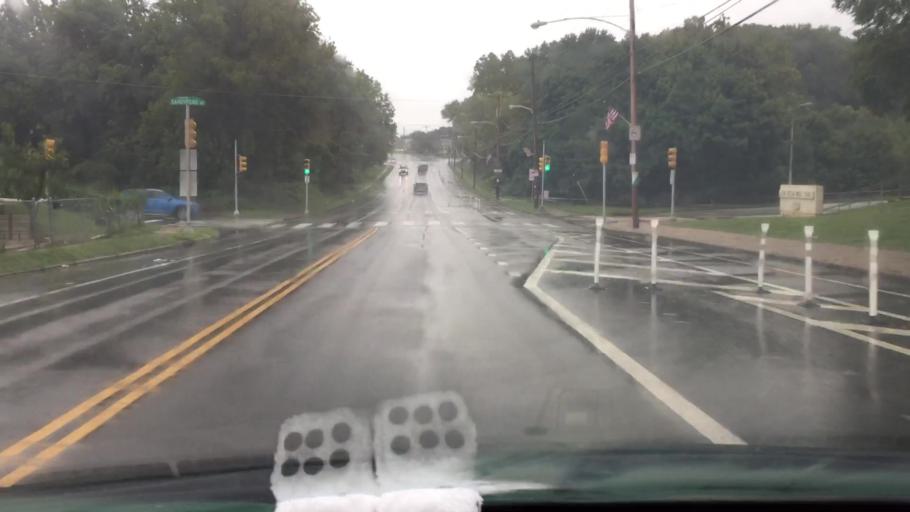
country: US
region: New Jersey
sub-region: Burlington County
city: Palmyra
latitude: 40.0461
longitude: -75.0453
